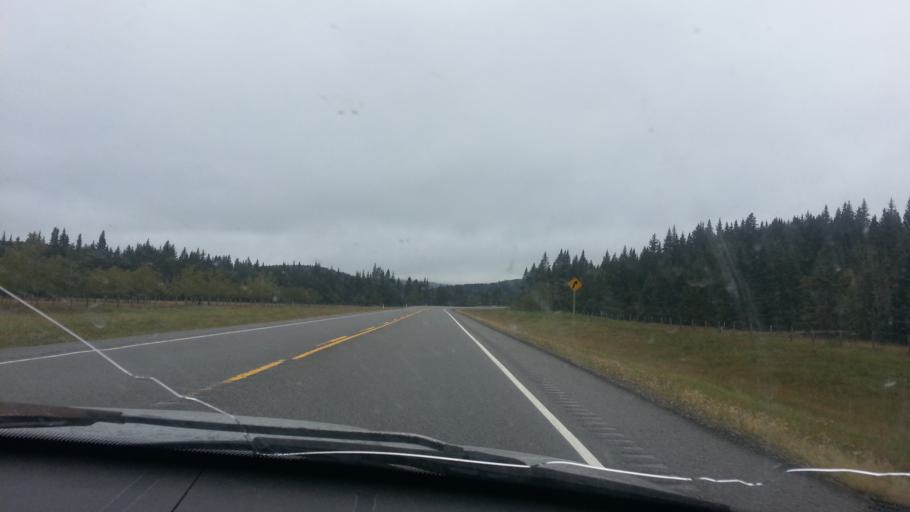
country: CA
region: Alberta
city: Cochrane
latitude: 51.0384
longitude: -114.7138
